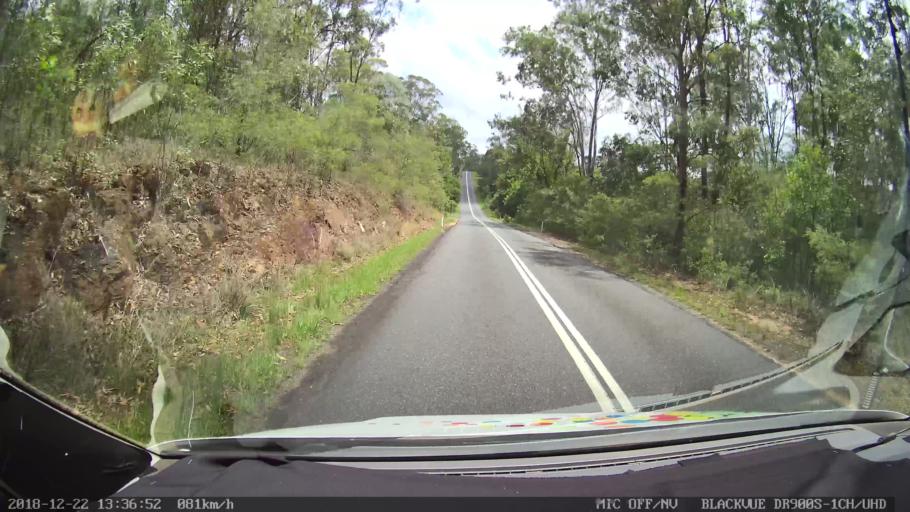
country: AU
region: New South Wales
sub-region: Clarence Valley
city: Coutts Crossing
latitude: -29.8842
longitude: 152.7915
